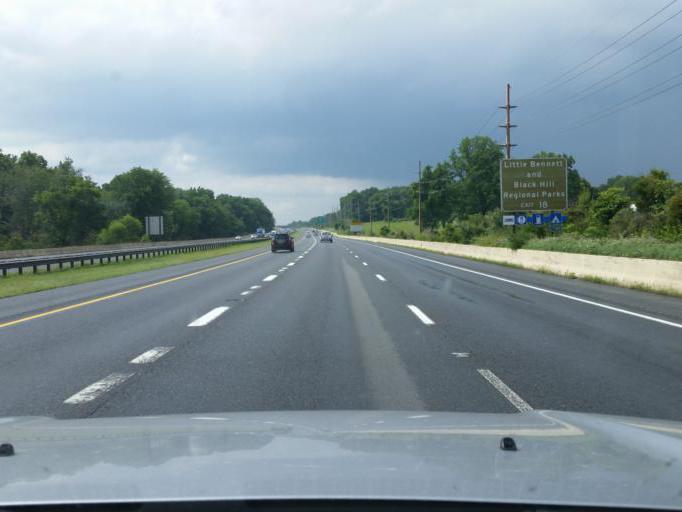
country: US
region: Maryland
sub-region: Montgomery County
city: Clarksburg
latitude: 39.2189
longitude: -77.2784
